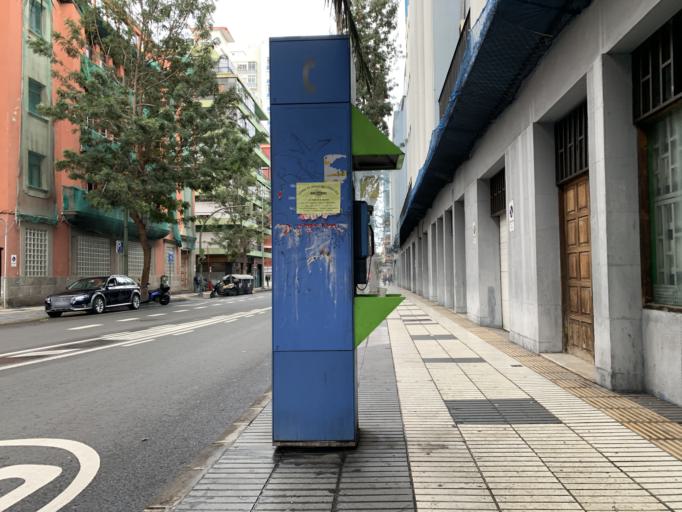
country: ES
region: Canary Islands
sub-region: Provincia de Las Palmas
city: Las Palmas de Gran Canaria
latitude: 28.1031
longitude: -15.4181
